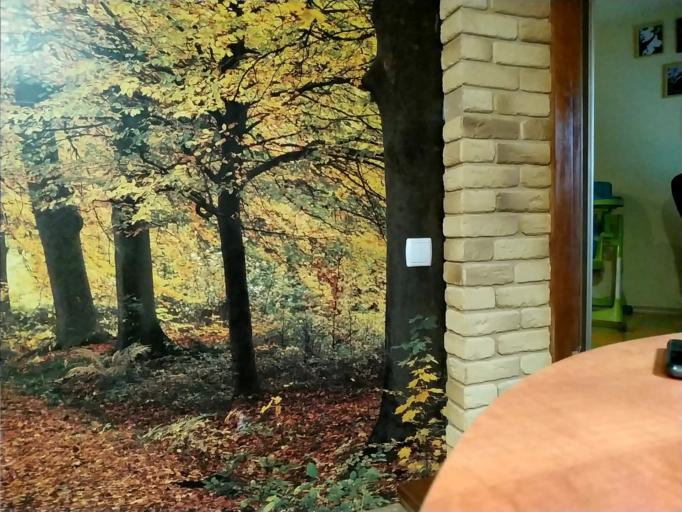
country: BY
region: Minsk
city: Il'ya
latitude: 54.4236
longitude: 27.5066
